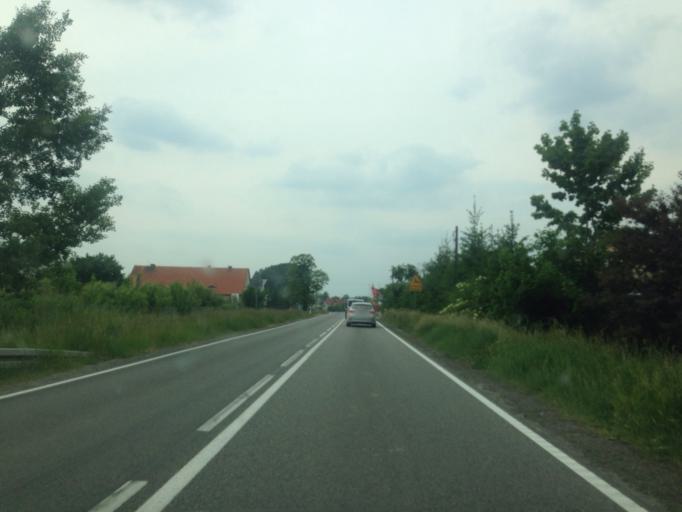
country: PL
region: Kujawsko-Pomorskie
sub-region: Powiat grudziadzki
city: Rogozno
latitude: 53.5021
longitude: 18.8685
